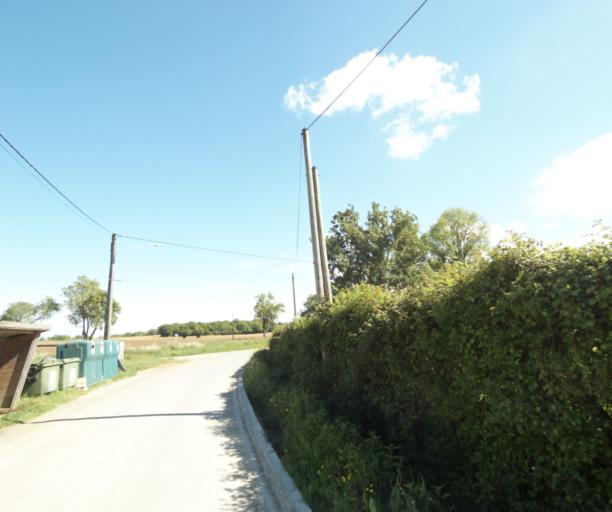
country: FR
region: Poitou-Charentes
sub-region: Departement de la Charente-Maritime
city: Saint-Georges-des-Coteaux
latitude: 45.7787
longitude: -0.6957
